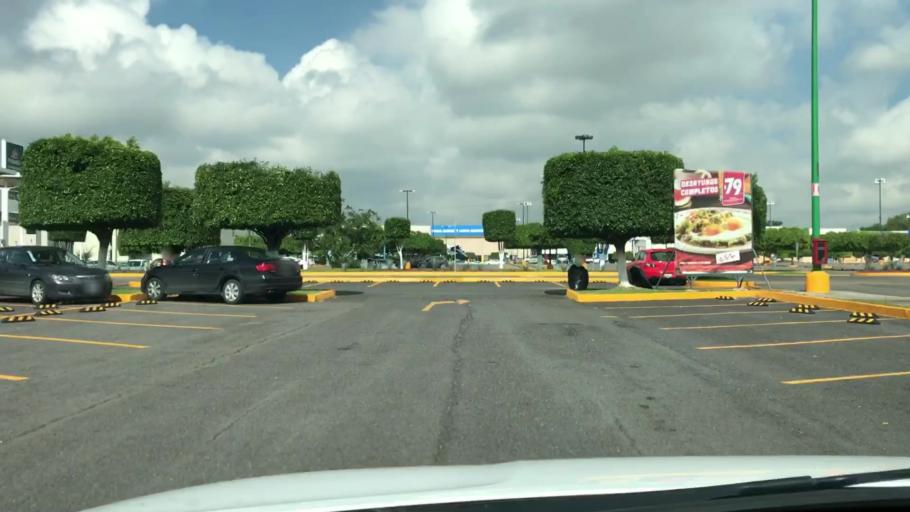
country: MX
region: Jalisco
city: Guadalajara
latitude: 20.6792
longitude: -103.4299
